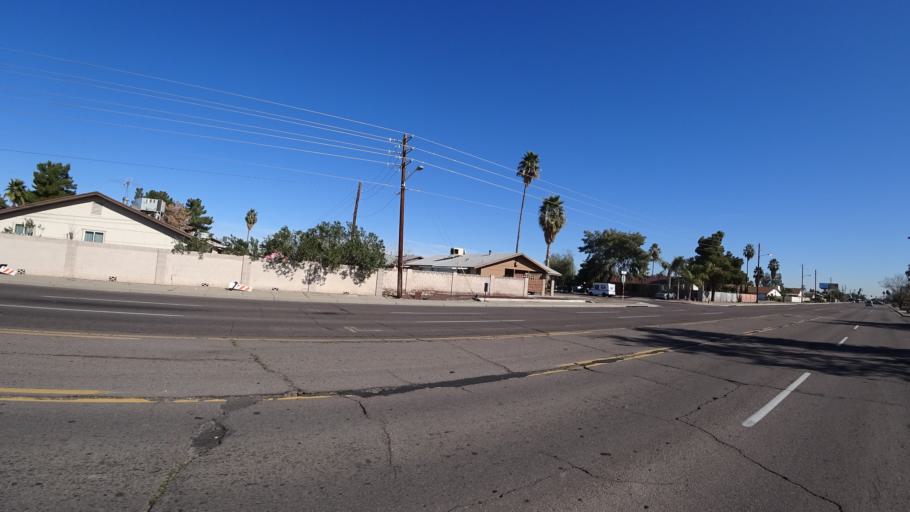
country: US
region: Arizona
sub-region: Maricopa County
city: Tolleson
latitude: 33.4942
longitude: -112.2430
